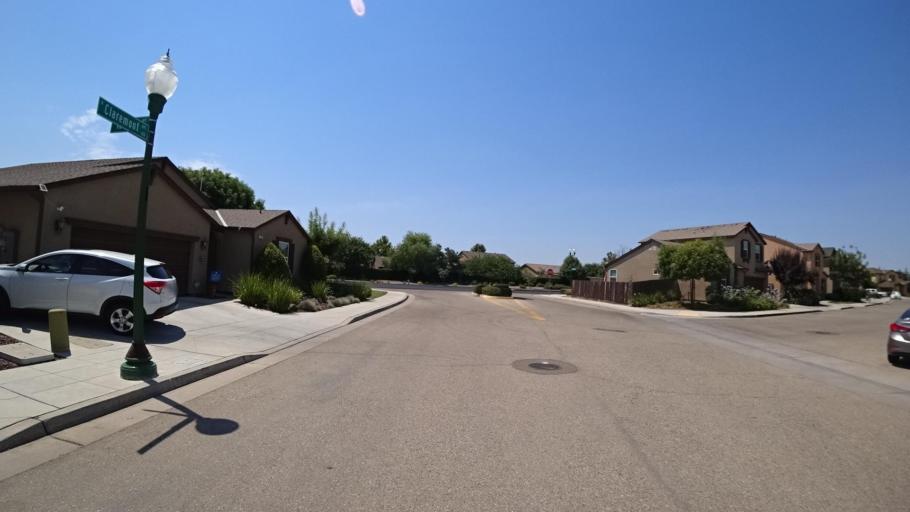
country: US
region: California
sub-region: Fresno County
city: Sunnyside
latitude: 36.7437
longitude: -119.6889
